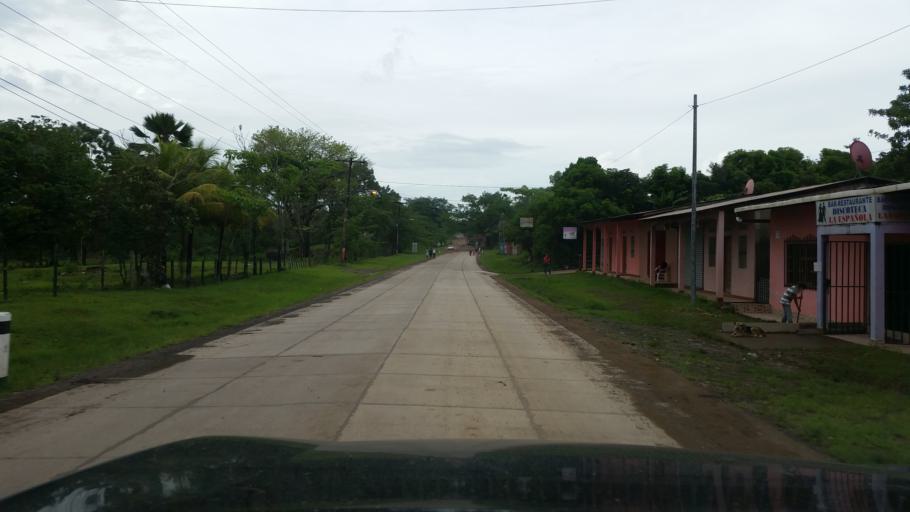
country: NI
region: Matagalpa
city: Rio Blanco
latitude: 13.1649
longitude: -84.9664
